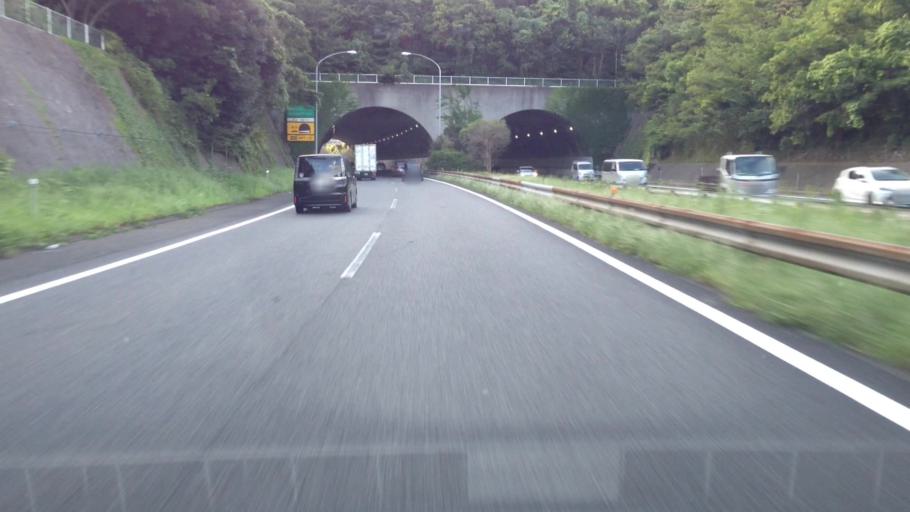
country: JP
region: Kanagawa
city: Zushi
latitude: 35.3220
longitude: 139.6031
